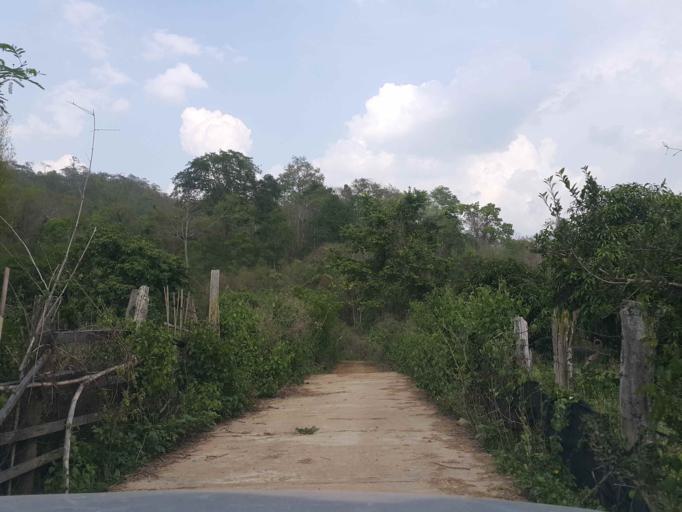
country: TH
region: Chiang Mai
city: Wiang Haeng
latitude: 19.3979
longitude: 98.7233
